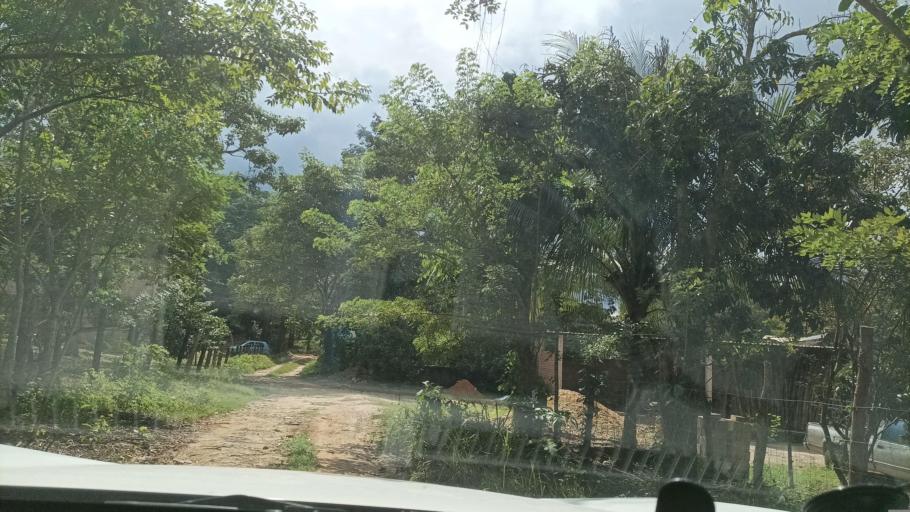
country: MX
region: Veracruz
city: Soconusco
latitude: 17.9670
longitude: -94.8854
